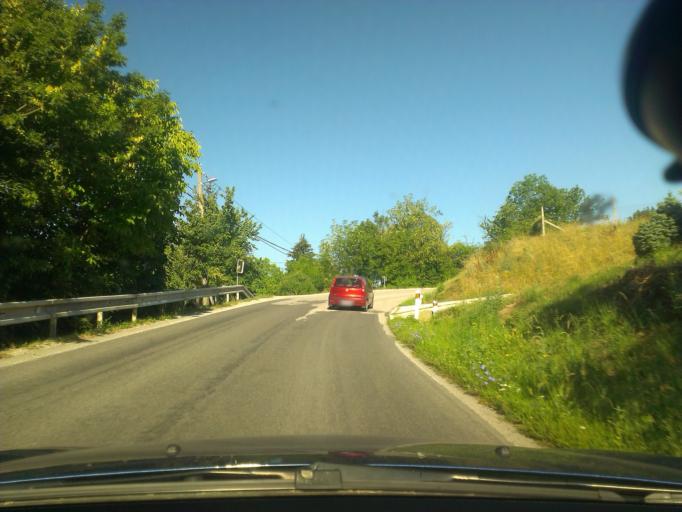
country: SK
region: Trnavsky
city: Vrbove
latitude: 48.6794
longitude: 17.6916
